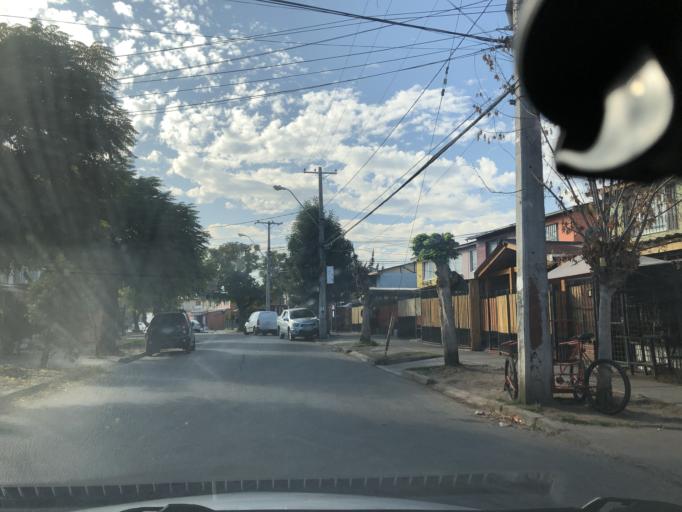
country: CL
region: Santiago Metropolitan
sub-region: Provincia de Cordillera
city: Puente Alto
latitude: -33.5896
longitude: -70.5637
